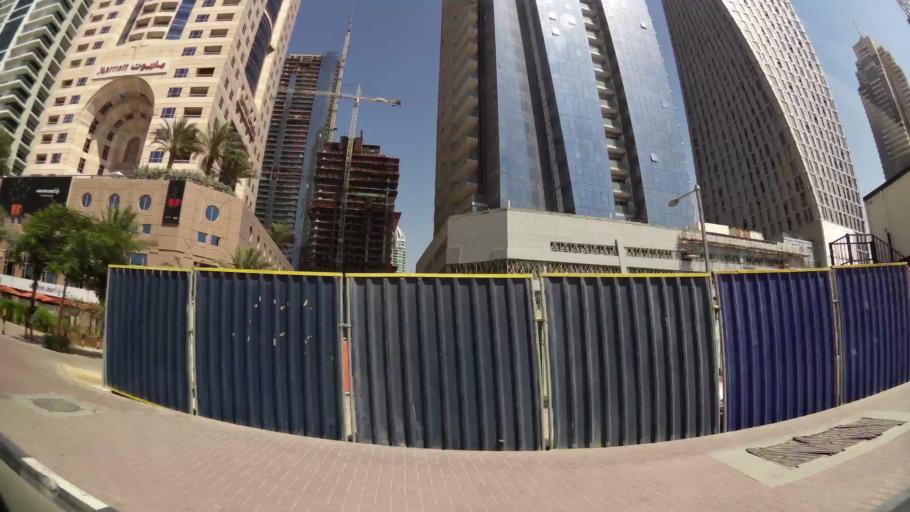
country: AE
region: Dubai
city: Dubai
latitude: 25.0879
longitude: 55.1451
